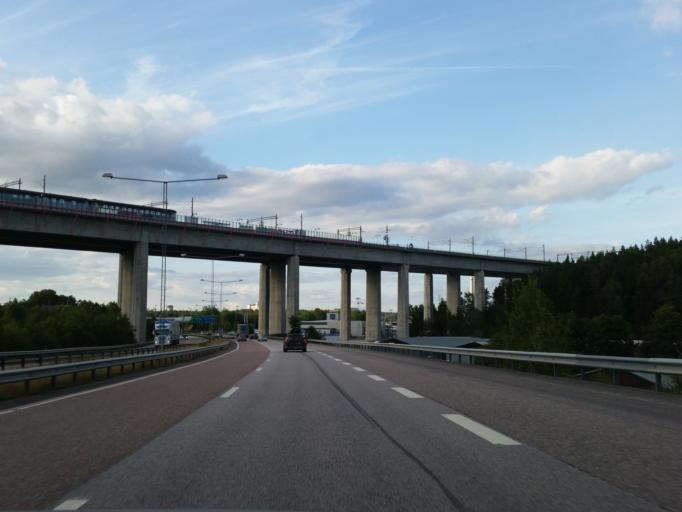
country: SE
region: Stockholm
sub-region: Sodertalje Kommun
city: Pershagen
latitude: 59.1616
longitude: 17.6490
